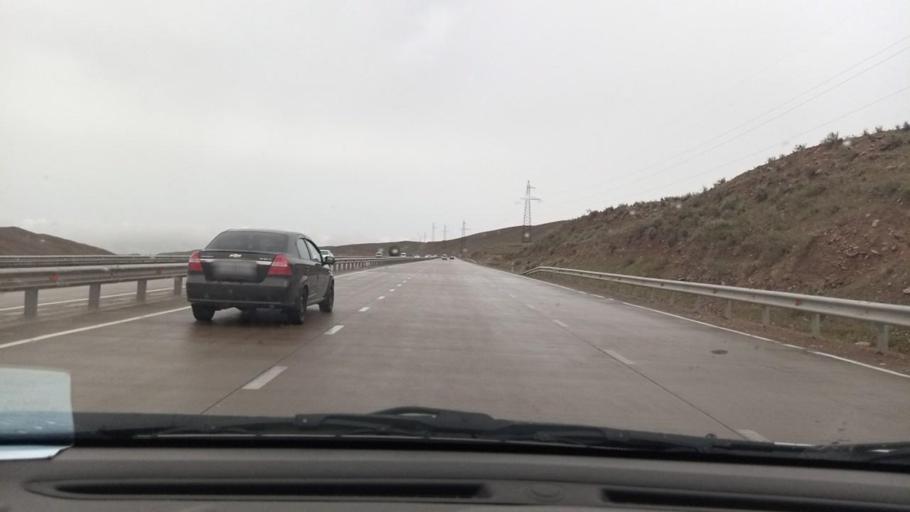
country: UZ
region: Namangan
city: Pop Shahri
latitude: 40.9399
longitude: 70.6911
